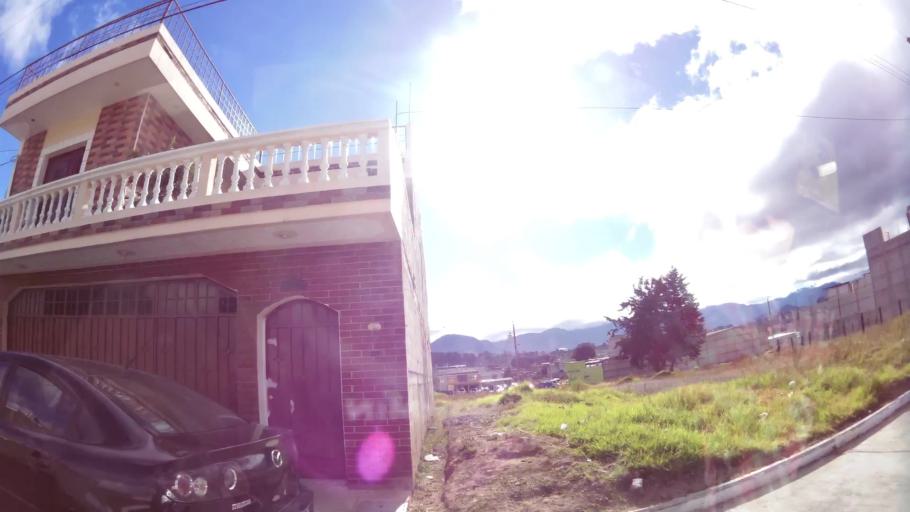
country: GT
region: Quetzaltenango
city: Salcaja
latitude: 14.8922
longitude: -91.4572
